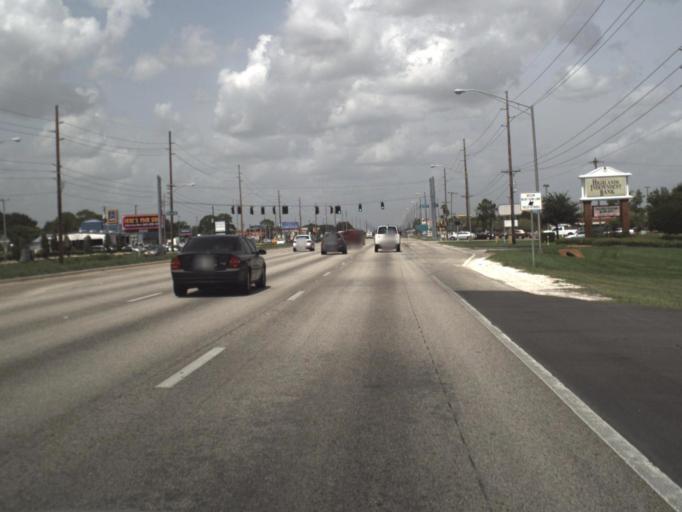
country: US
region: Florida
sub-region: Highlands County
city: Sebring
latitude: 27.5068
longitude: -81.4920
